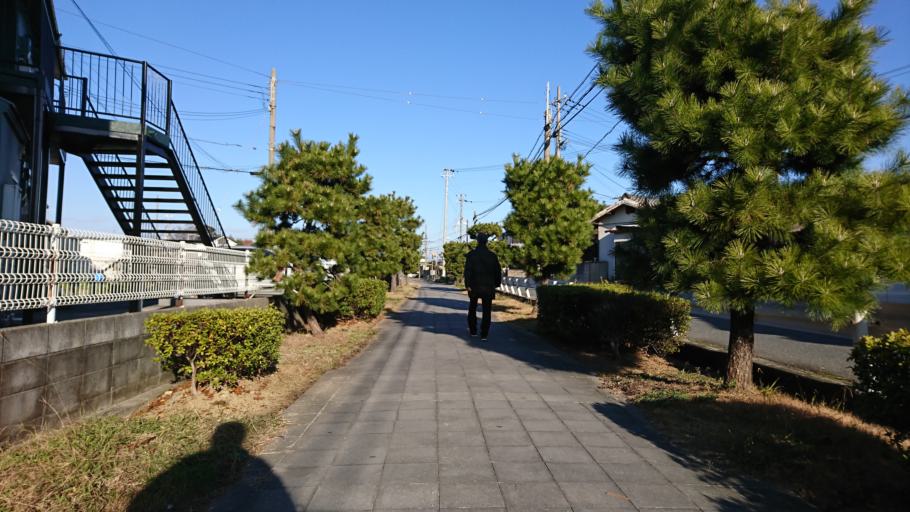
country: JP
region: Hyogo
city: Kakogawacho-honmachi
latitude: 34.7431
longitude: 134.8444
